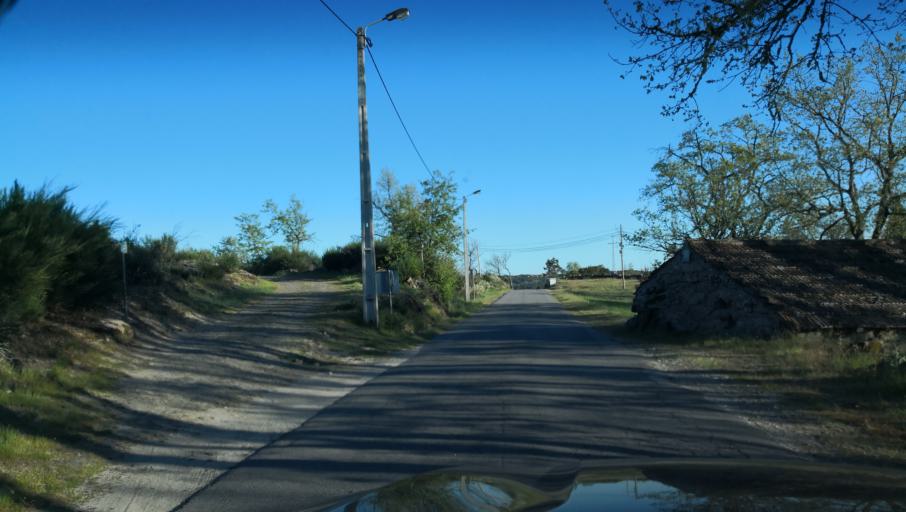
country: PT
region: Vila Real
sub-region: Vila Real
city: Vila Real
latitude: 41.3589
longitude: -7.6506
